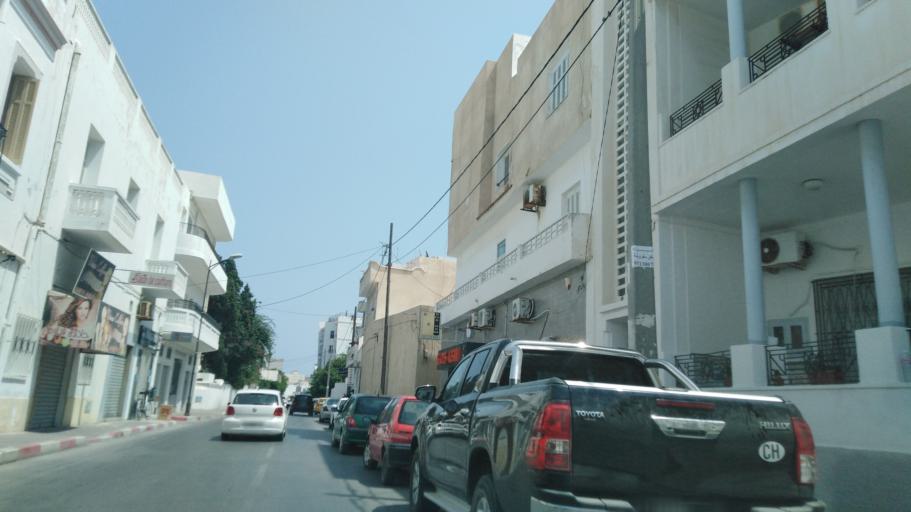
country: TN
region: Al Mahdiyah
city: Mahdia
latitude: 35.5061
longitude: 11.0603
